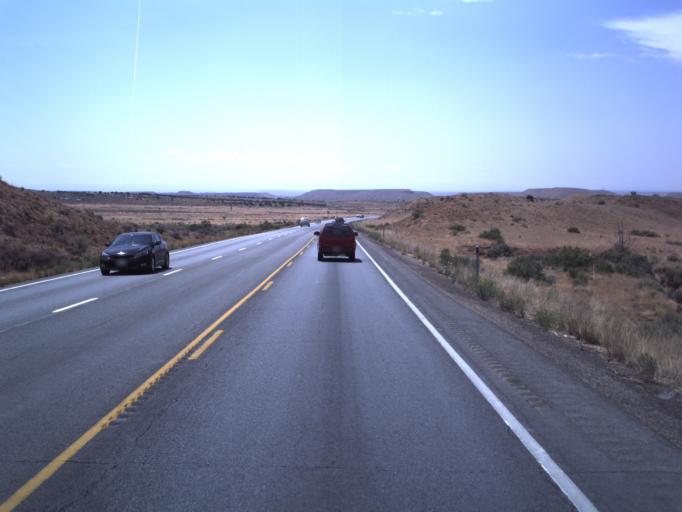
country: US
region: Utah
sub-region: Uintah County
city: Maeser
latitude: 40.4007
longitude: -109.5917
